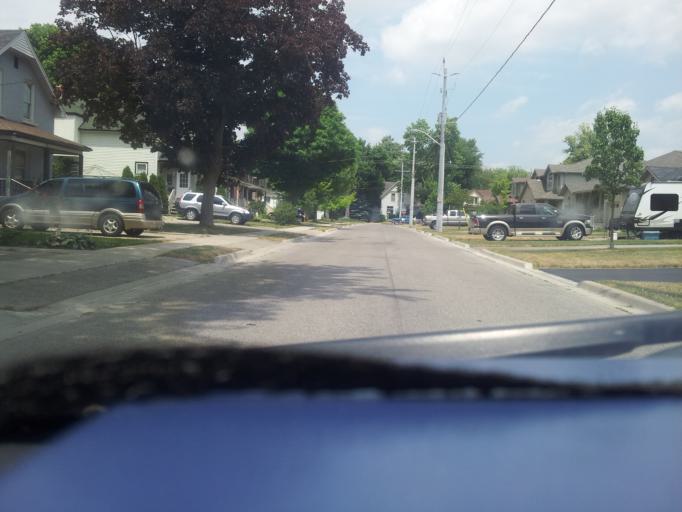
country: CA
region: Ontario
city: Stratford
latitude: 43.3684
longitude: -80.9689
